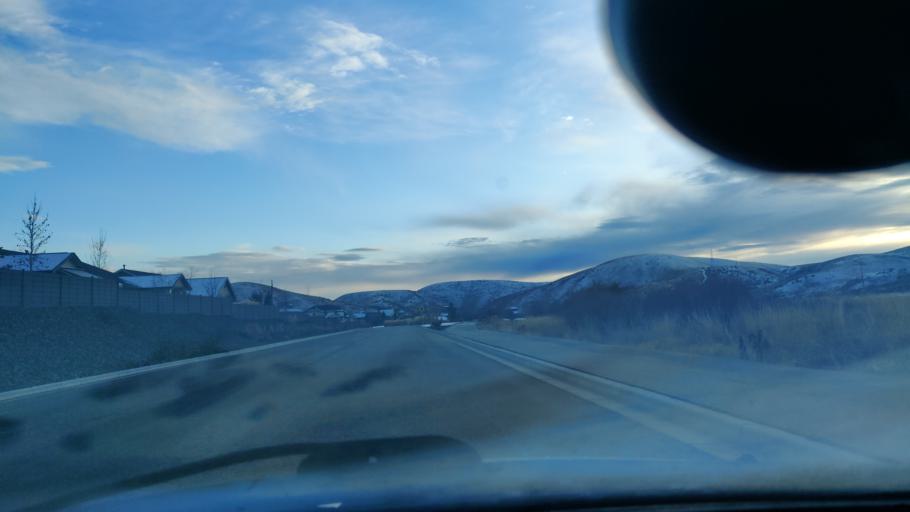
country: US
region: Idaho
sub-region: Ada County
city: Eagle
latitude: 43.7791
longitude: -116.2623
